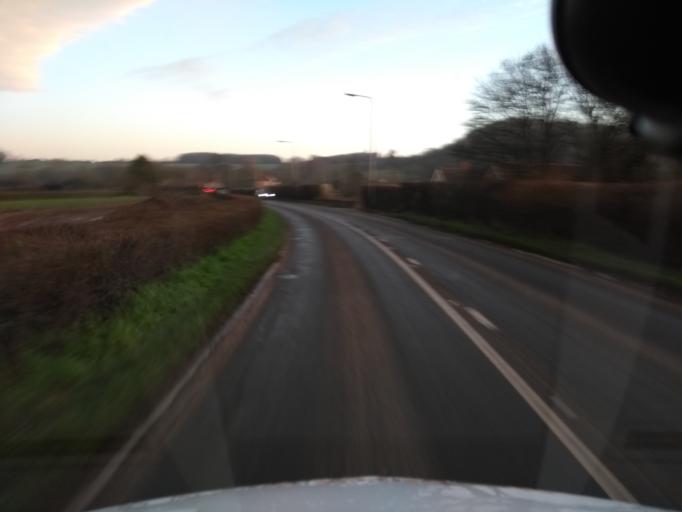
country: GB
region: England
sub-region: Somerset
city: Puriton
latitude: 51.1526
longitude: -2.9595
